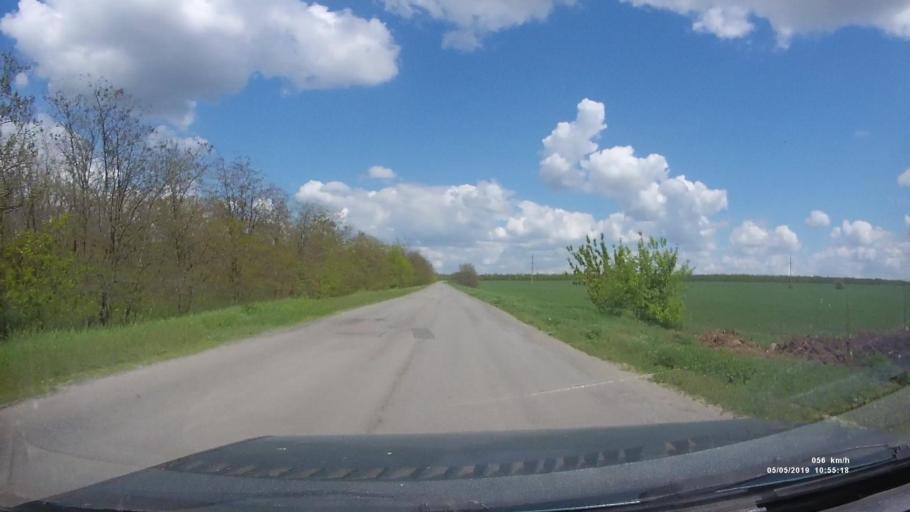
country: RU
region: Rostov
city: Ust'-Donetskiy
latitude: 47.6644
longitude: 40.8214
